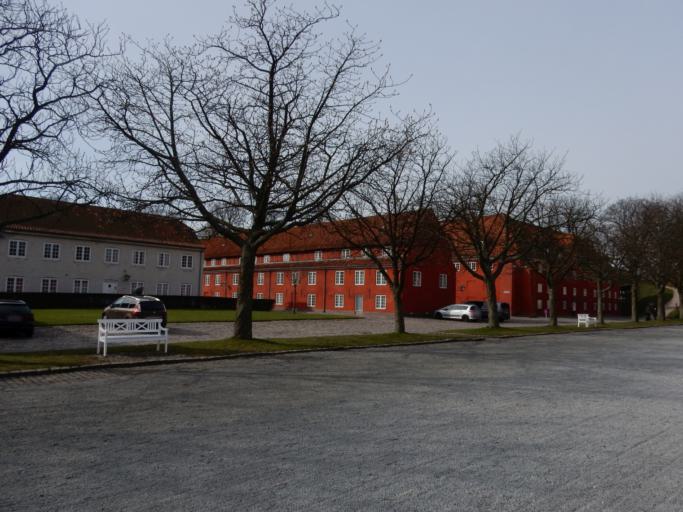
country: DK
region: Capital Region
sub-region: Kobenhavn
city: Christianshavn
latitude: 55.6914
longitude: 12.5947
